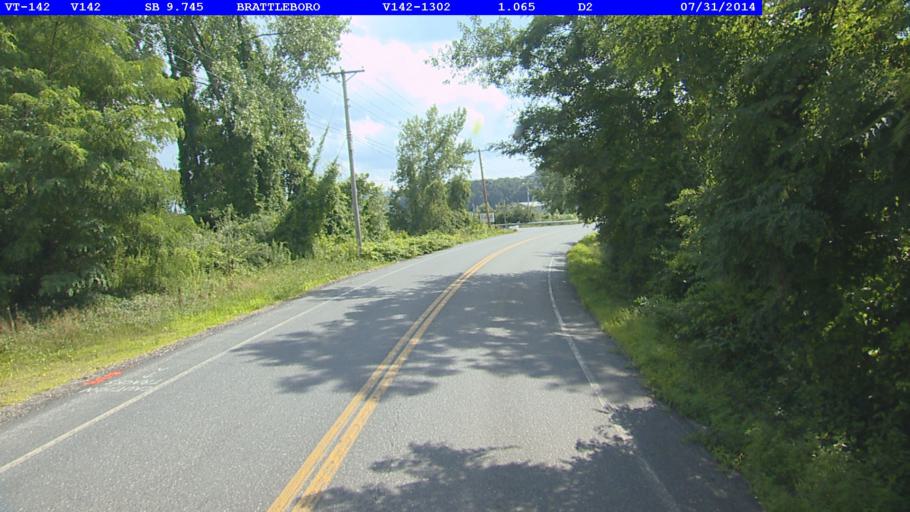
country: US
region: Vermont
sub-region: Windham County
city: Brattleboro
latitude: 42.8365
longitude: -72.5494
